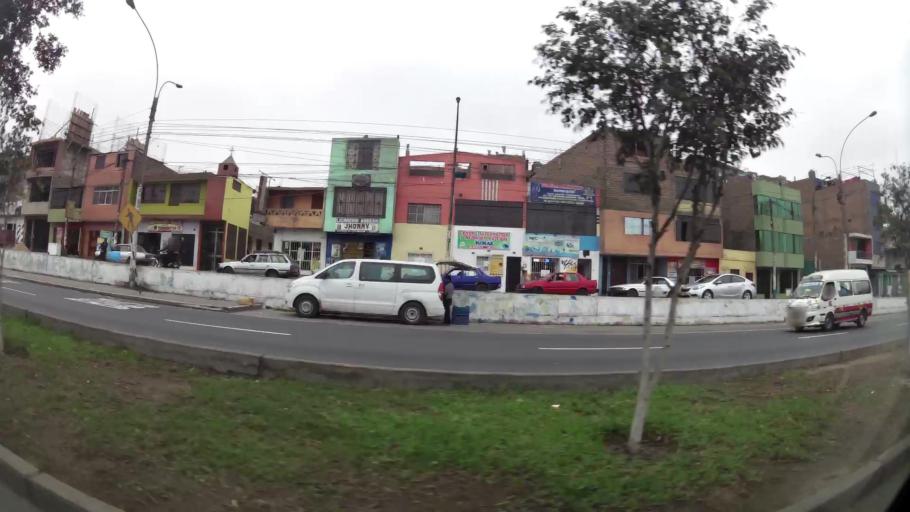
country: PE
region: Lima
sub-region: Lima
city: Independencia
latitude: -11.9605
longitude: -77.0539
